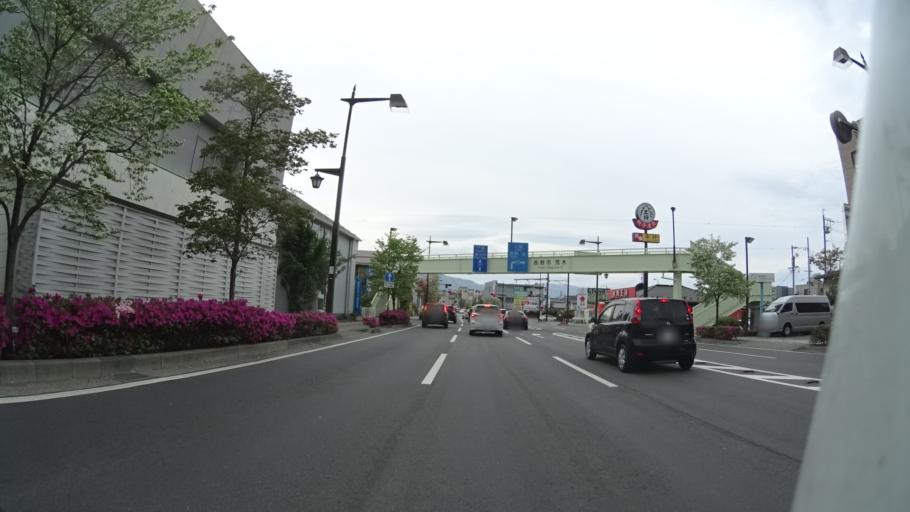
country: JP
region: Nagano
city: Nagano-shi
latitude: 36.6276
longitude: 138.1830
